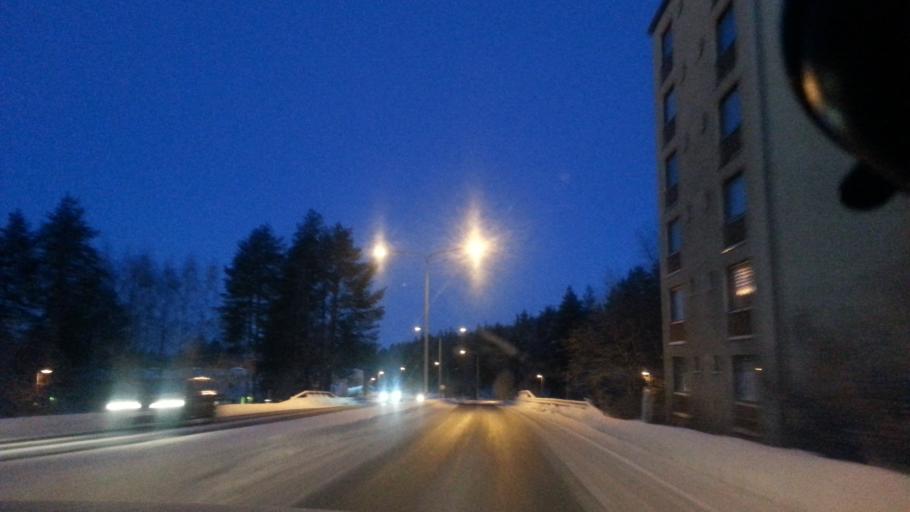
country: FI
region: Lapland
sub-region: Rovaniemi
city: Rovaniemi
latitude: 66.4984
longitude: 25.7563
